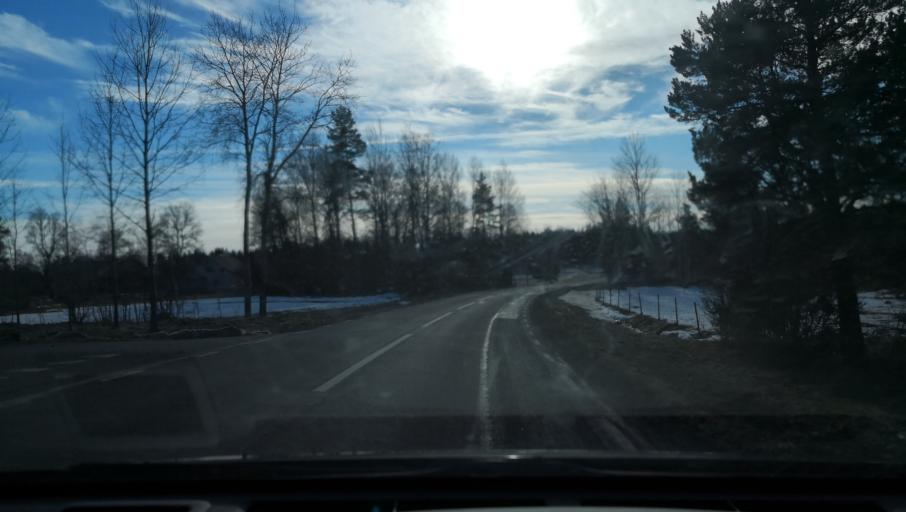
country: SE
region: Uppsala
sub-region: Osthammars Kommun
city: Osterbybruk
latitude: 60.2830
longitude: 17.9783
